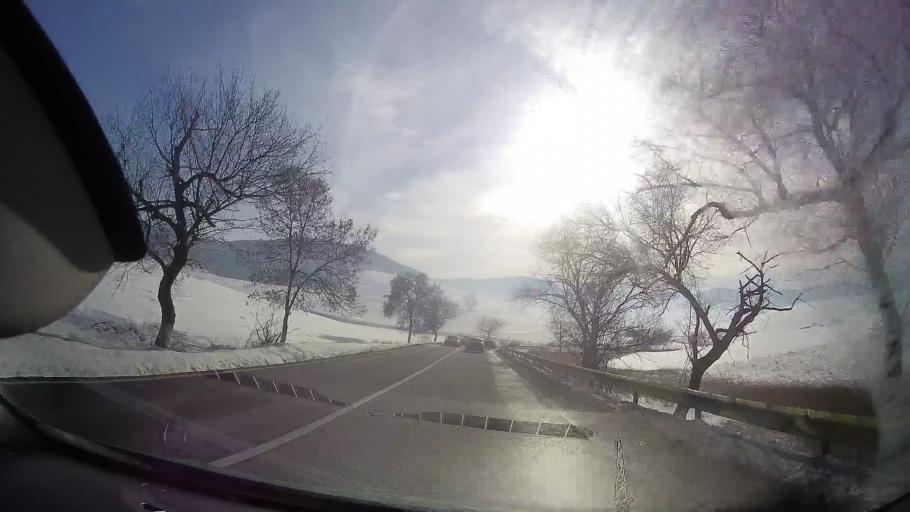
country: RO
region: Neamt
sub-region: Comuna Garcina
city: Garcina
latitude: 46.9935
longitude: 26.3644
